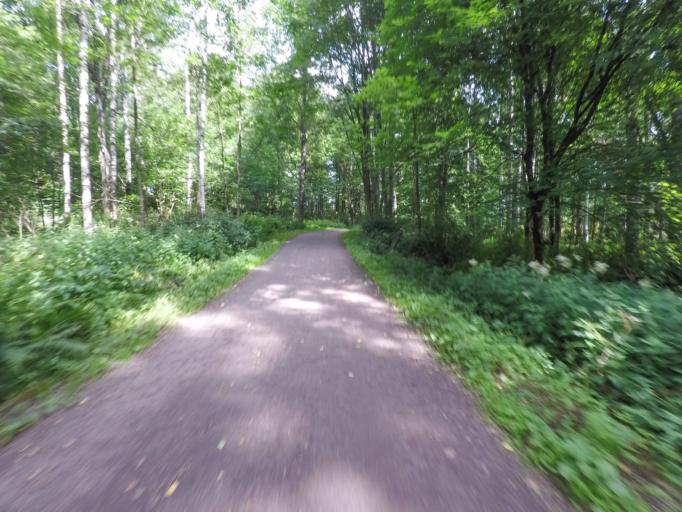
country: FI
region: Uusimaa
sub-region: Helsinki
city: Vantaa
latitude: 60.2198
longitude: 25.0085
